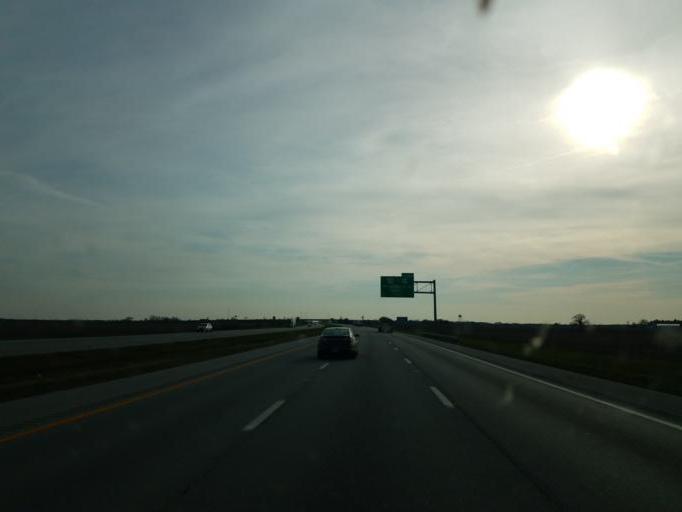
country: US
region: Ohio
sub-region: Fayette County
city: Jeffersonville
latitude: 39.6311
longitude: -83.5866
